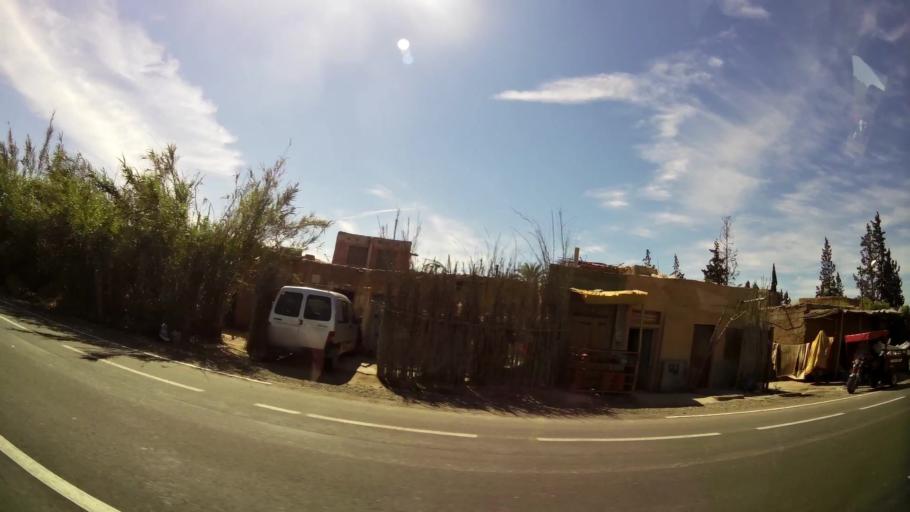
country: MA
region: Marrakech-Tensift-Al Haouz
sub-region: Marrakech
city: Marrakesh
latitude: 31.6455
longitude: -8.1053
